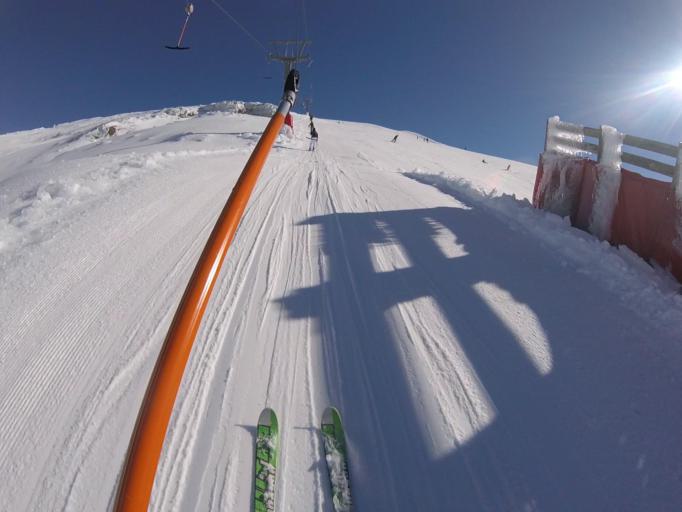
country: ES
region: Andalusia
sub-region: Provincia de Granada
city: Capileira
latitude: 37.0612
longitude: -3.3761
